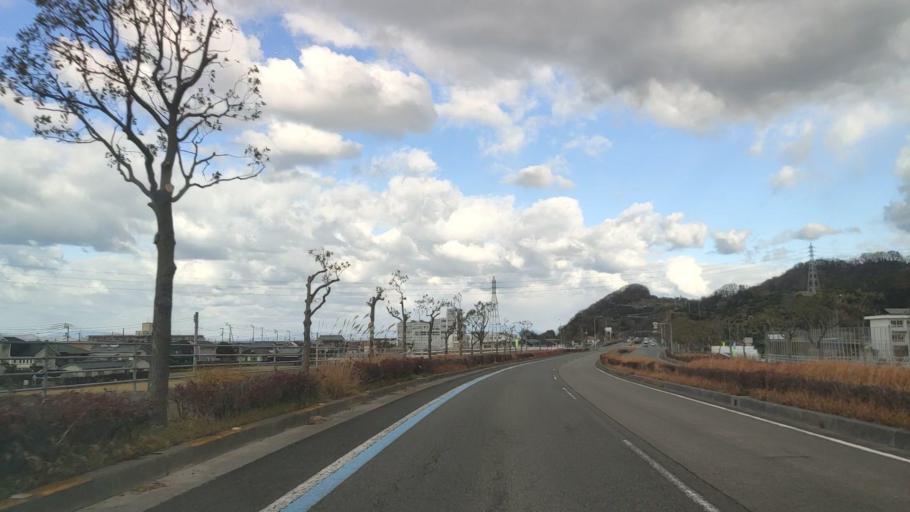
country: JP
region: Ehime
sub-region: Shikoku-chuo Shi
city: Matsuyama
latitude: 33.9004
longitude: 132.7571
